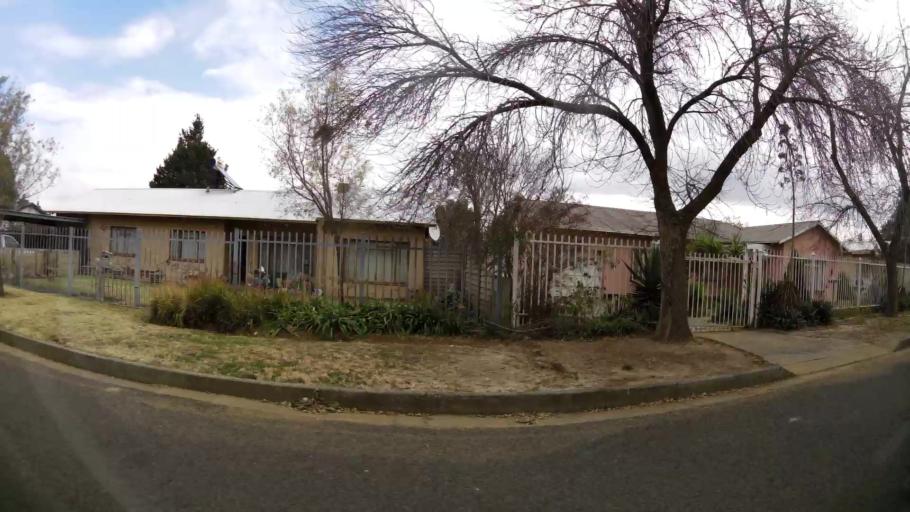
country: ZA
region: Orange Free State
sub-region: Fezile Dabi District Municipality
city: Kroonstad
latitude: -27.6395
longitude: 27.2290
